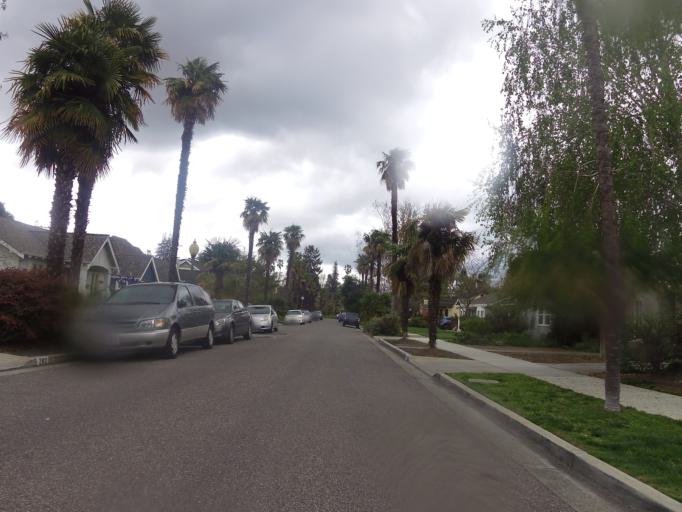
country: US
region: California
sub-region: Santa Clara County
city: Mountain View
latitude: 37.3894
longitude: -122.0743
